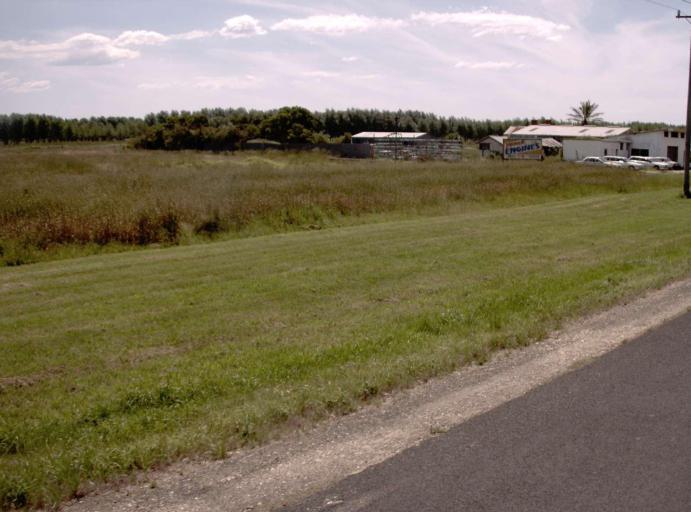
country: AU
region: Victoria
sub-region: Wellington
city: Sale
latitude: -38.0573
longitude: 147.0690
